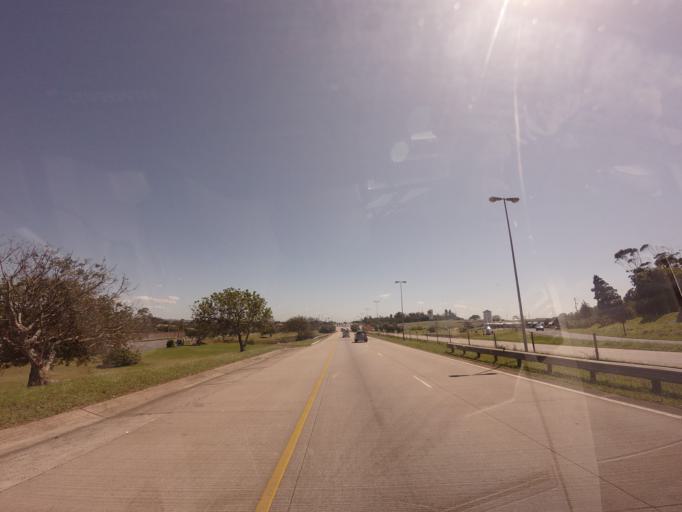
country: ZA
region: KwaZulu-Natal
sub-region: iLembe District Municipality
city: Stanger
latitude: -29.4074
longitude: 31.2827
